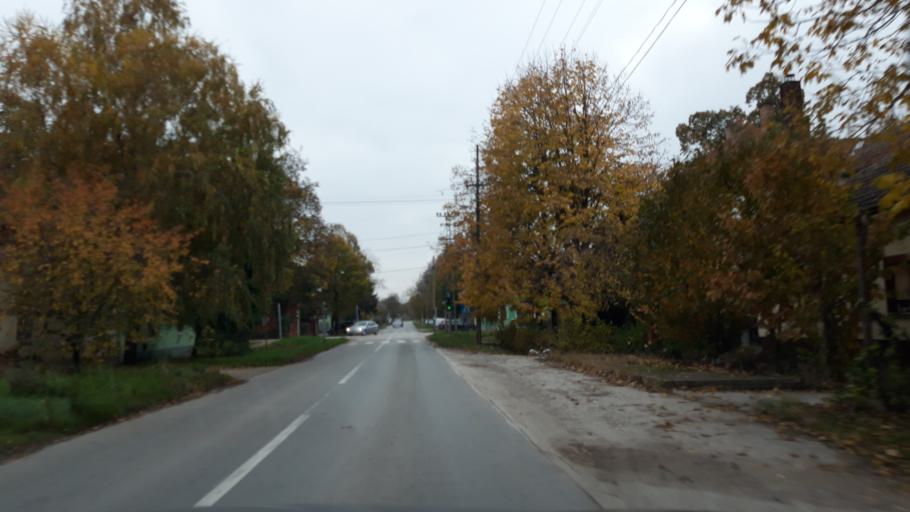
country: RS
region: Autonomna Pokrajina Vojvodina
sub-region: Severnobanatski Okrug
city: Novi Knezevac
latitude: 46.0421
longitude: 20.0968
